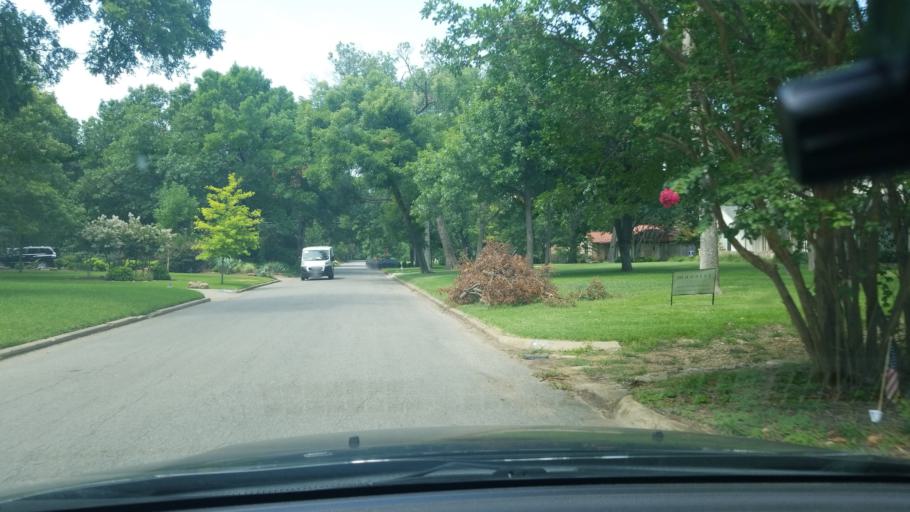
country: US
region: Texas
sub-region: Dallas County
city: Highland Park
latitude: 32.8123
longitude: -96.7170
